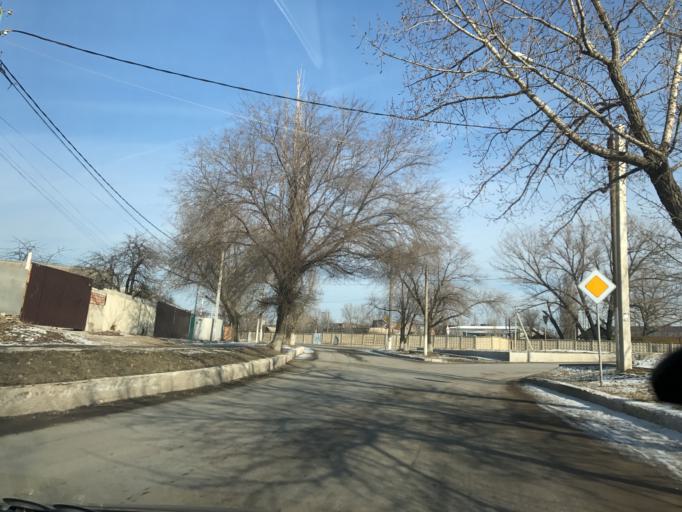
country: RU
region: Rostov
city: Kamensk-Shakhtinskiy
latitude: 48.3186
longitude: 40.2562
